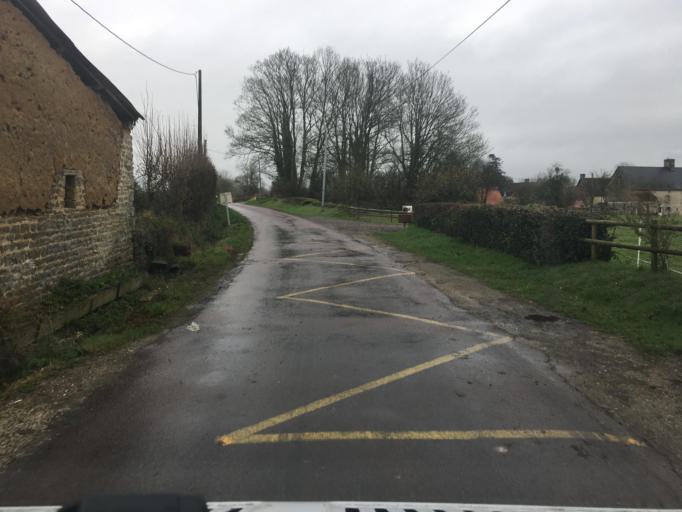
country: FR
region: Lower Normandy
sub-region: Departement de la Manche
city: Sainte-Mere-Eglise
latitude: 49.4269
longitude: -1.2644
